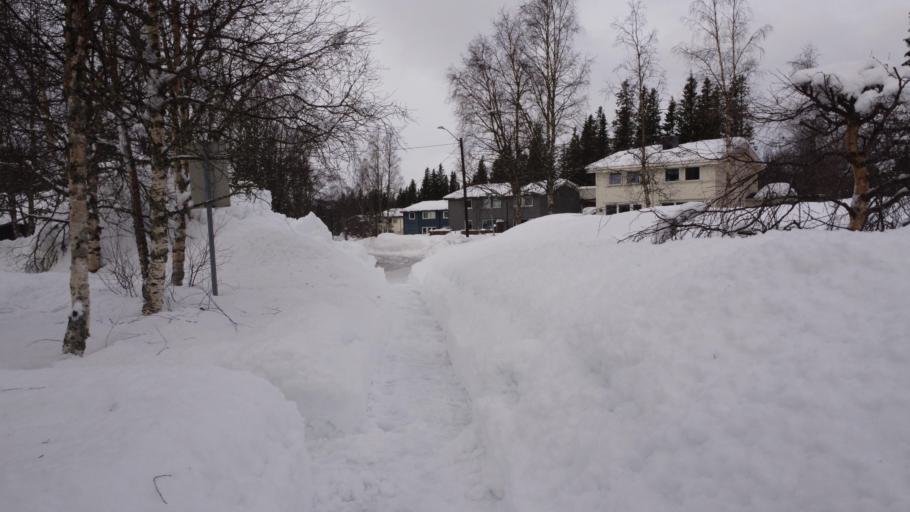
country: NO
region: Nordland
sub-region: Rana
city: Mo i Rana
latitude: 66.3348
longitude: 14.1513
